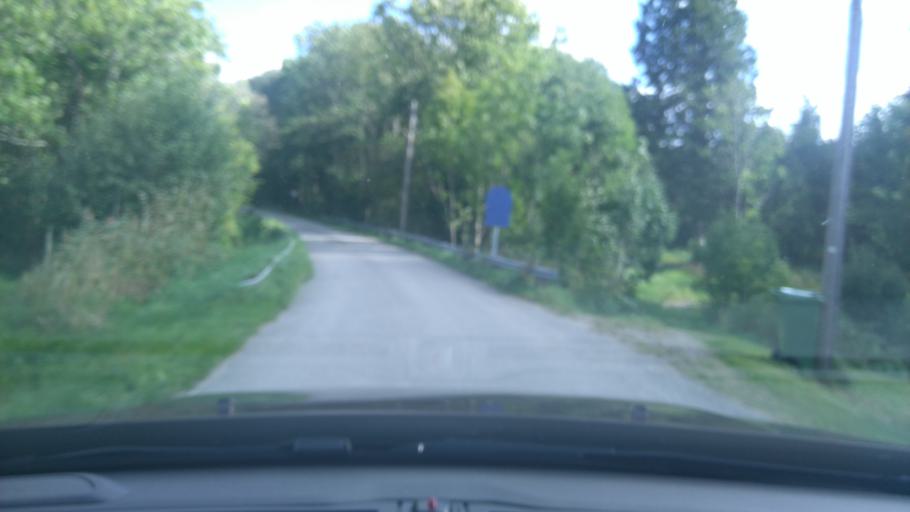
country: SE
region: Vaestra Goetaland
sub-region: Lilla Edets Kommun
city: Lodose
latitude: 58.0441
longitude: 12.1536
